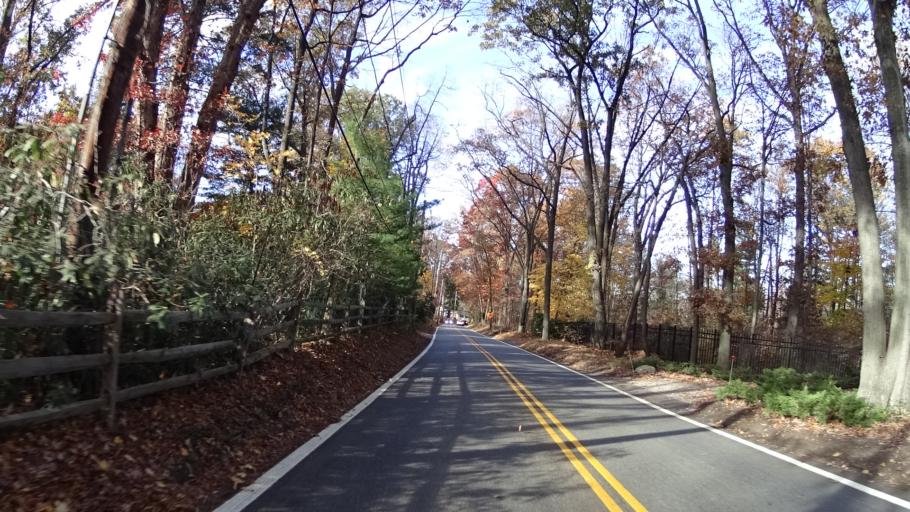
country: US
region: New Jersey
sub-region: Morris County
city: Morristown
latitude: 40.7393
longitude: -74.5011
